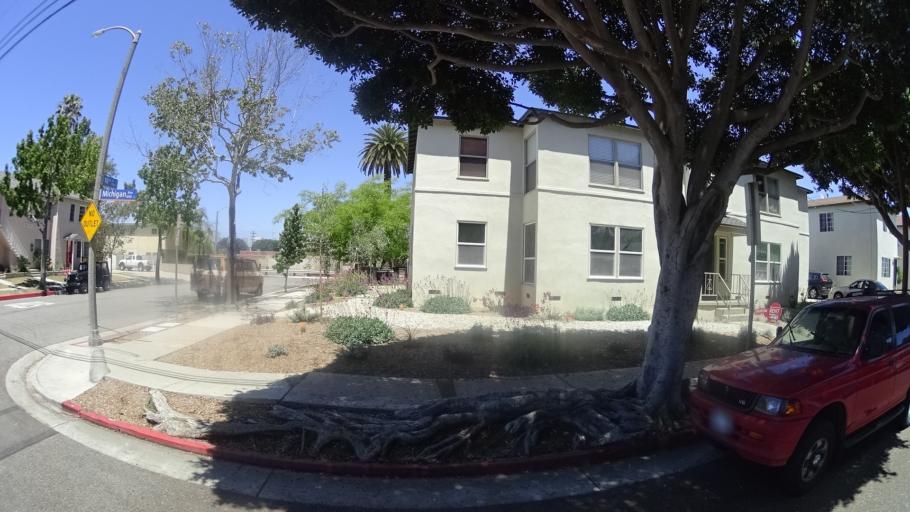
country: US
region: California
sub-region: Los Angeles County
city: Santa Monica
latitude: 34.0216
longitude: -118.4753
